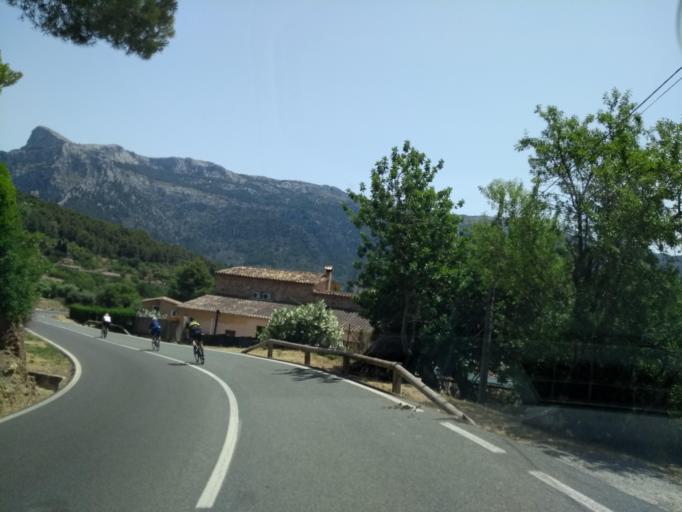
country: ES
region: Balearic Islands
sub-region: Illes Balears
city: Soller
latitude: 39.7827
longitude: 2.7106
